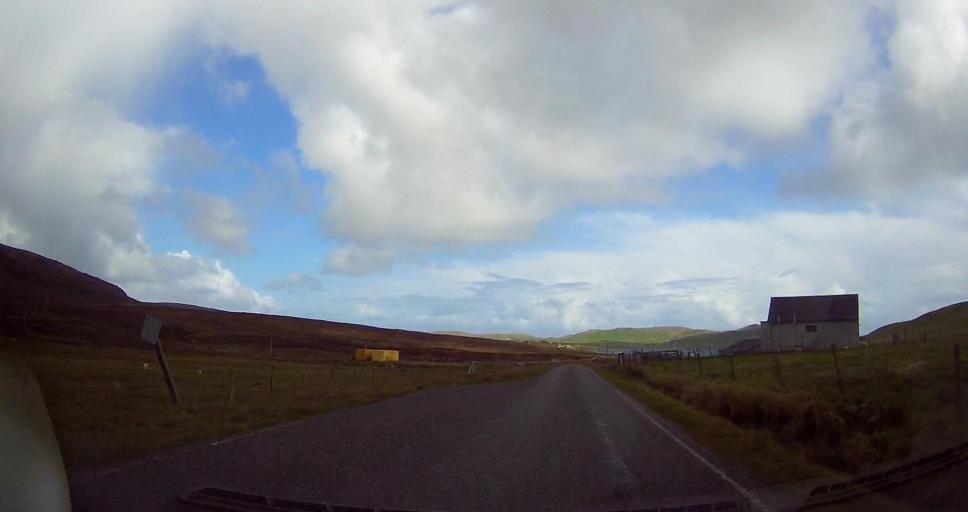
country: GB
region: Scotland
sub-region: Shetland Islands
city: Lerwick
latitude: 60.5705
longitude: -1.3335
